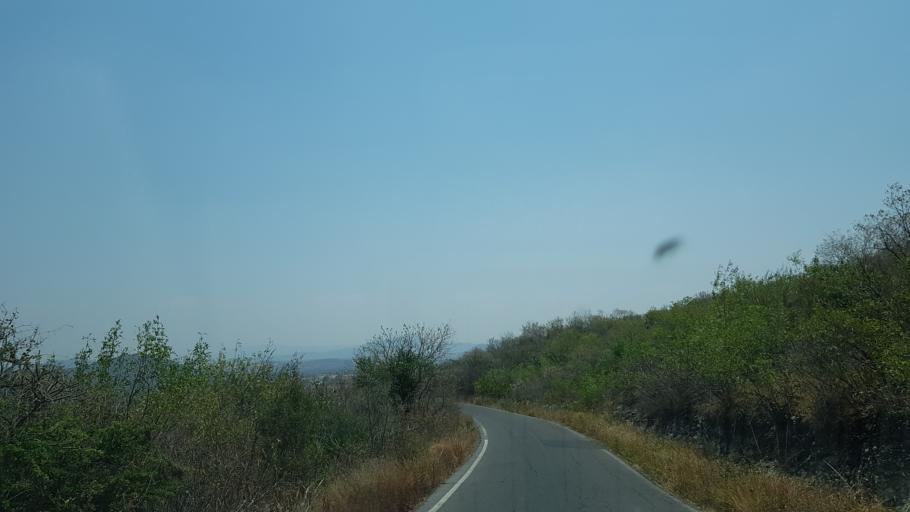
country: MX
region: Puebla
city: Huaquechula
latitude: 18.7928
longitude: -98.5450
